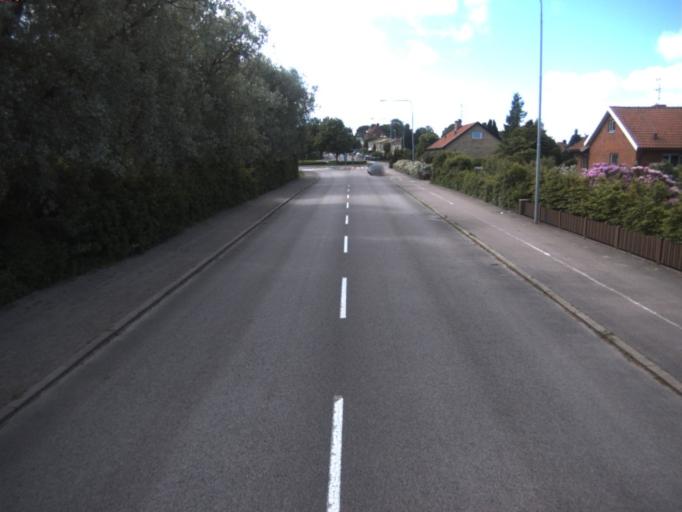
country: SE
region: Skane
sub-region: Helsingborg
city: Helsingborg
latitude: 56.0665
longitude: 12.6991
